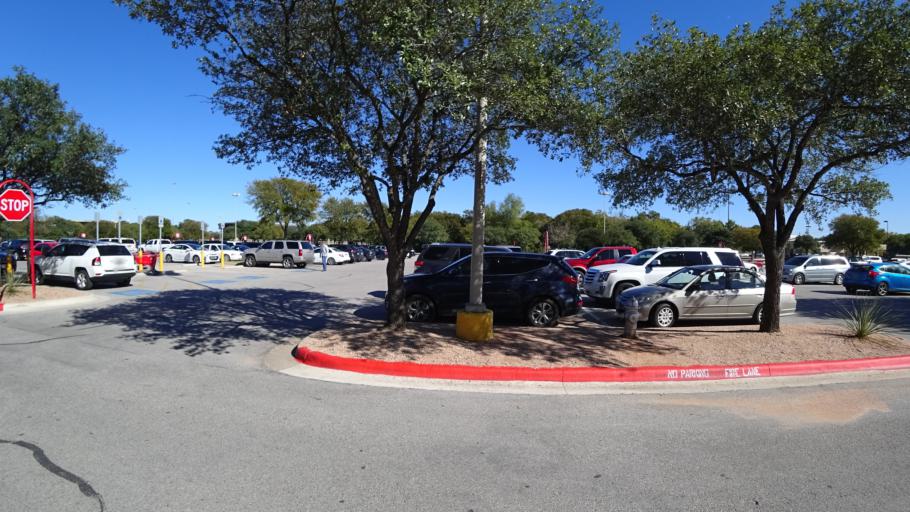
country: US
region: Texas
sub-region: Travis County
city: Rollingwood
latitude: 30.2337
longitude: -97.8284
